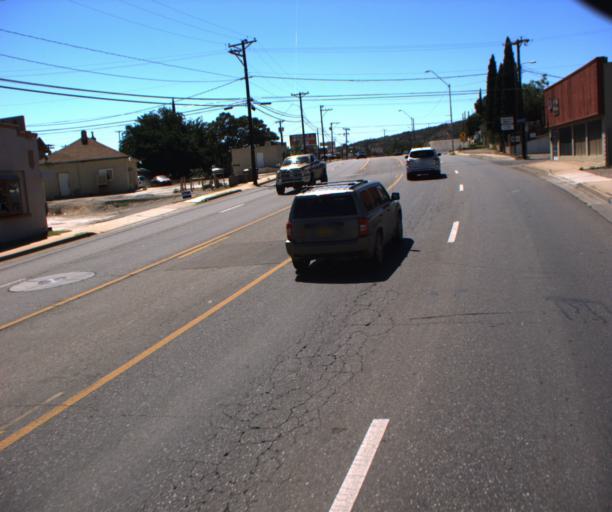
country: US
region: Arizona
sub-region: Gila County
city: Globe
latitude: 33.4005
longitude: -110.7915
